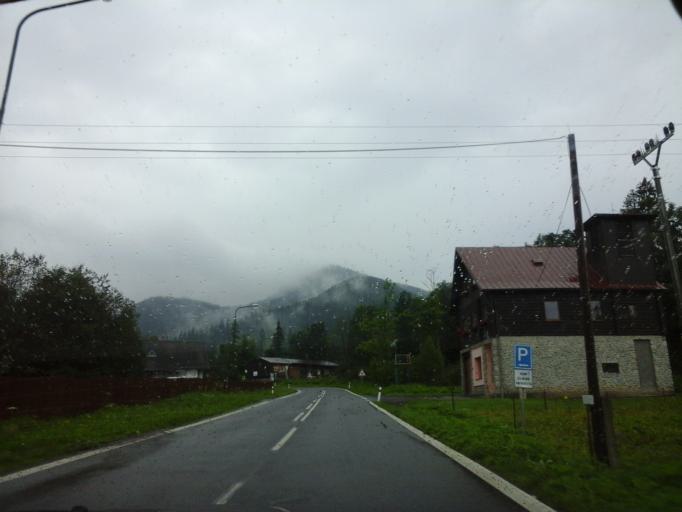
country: PL
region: Lesser Poland Voivodeship
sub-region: Powiat tatrzanski
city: Bukowina Tatrzanska
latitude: 49.2672
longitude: 20.1424
